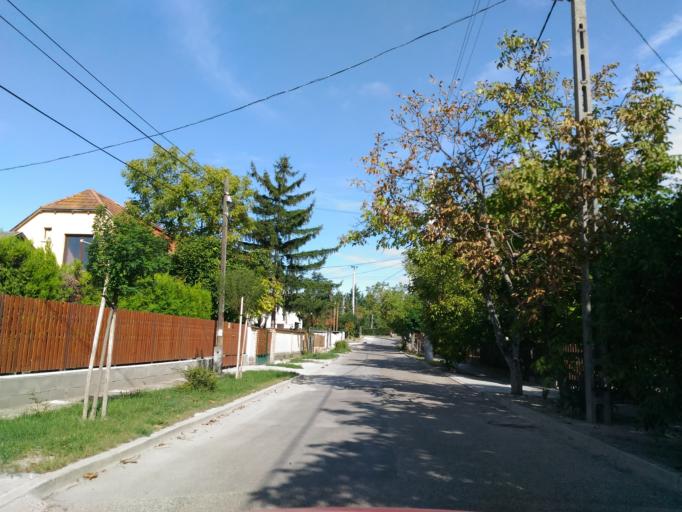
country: HU
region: Pest
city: Diosd
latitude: 47.4044
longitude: 18.9819
